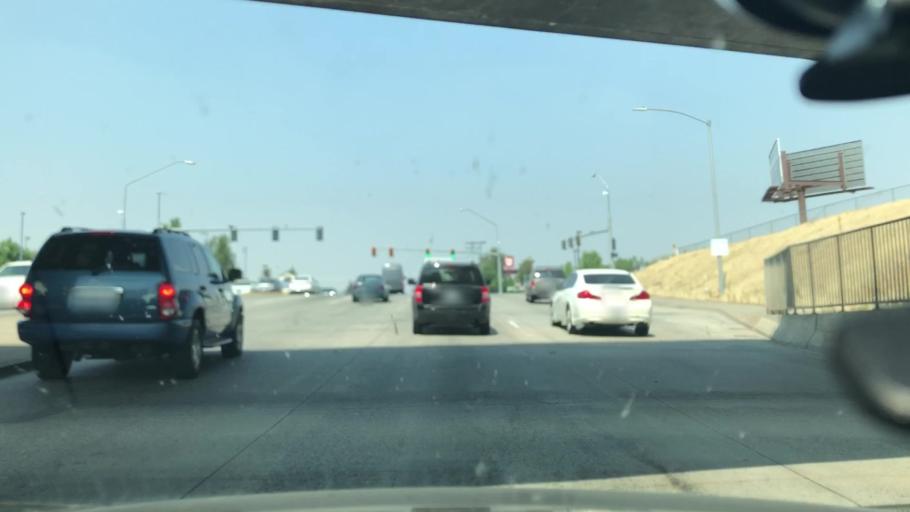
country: US
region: Washington
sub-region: Spokane County
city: Millwood
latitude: 47.6803
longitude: -117.2827
